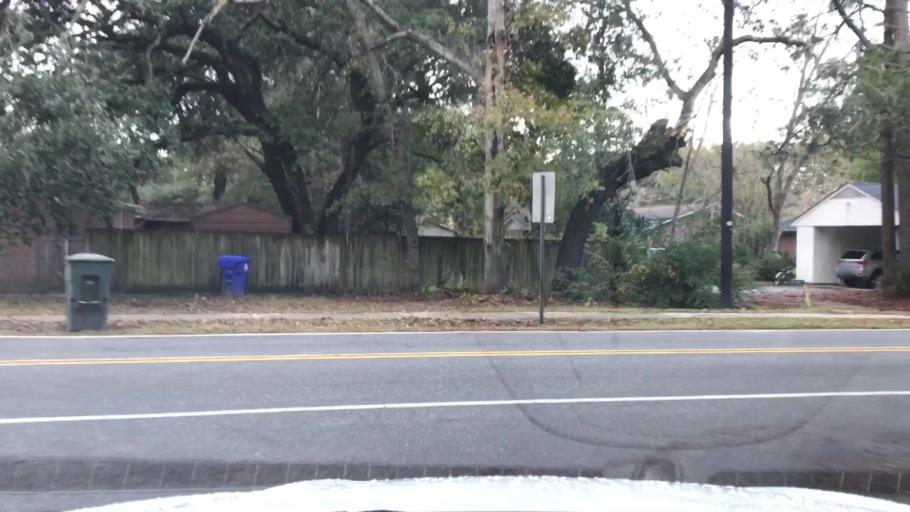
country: US
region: South Carolina
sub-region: Charleston County
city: North Charleston
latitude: 32.8175
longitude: -79.9975
